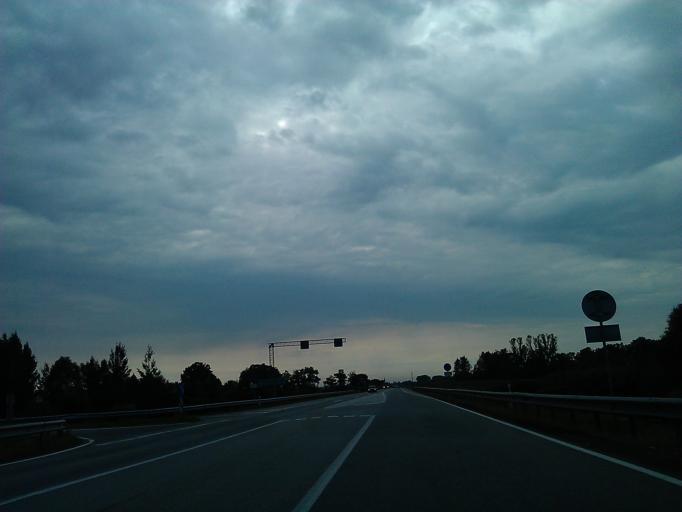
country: LV
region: Lecava
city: Iecava
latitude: 56.6243
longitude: 24.2199
